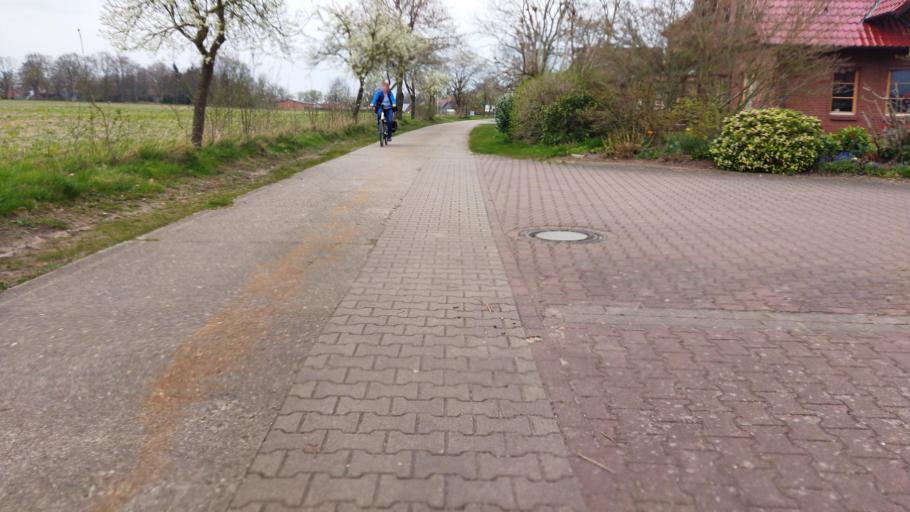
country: DE
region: Lower Saxony
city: Estorf
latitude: 52.5865
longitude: 9.1345
